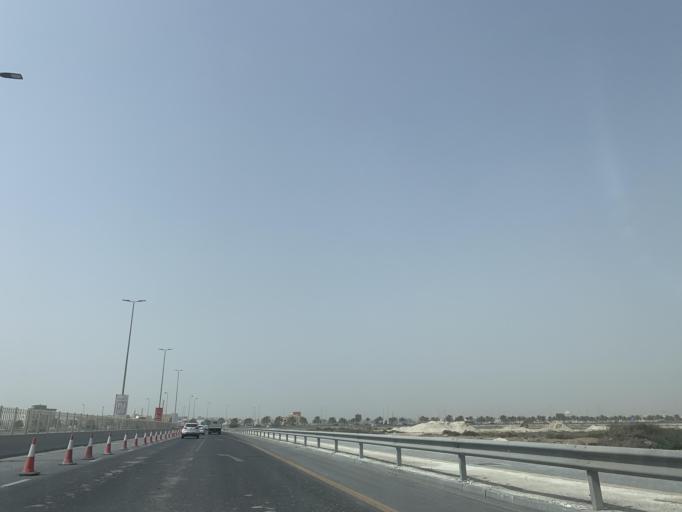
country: BH
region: Northern
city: Madinat `Isa
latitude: 26.1887
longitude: 50.5187
